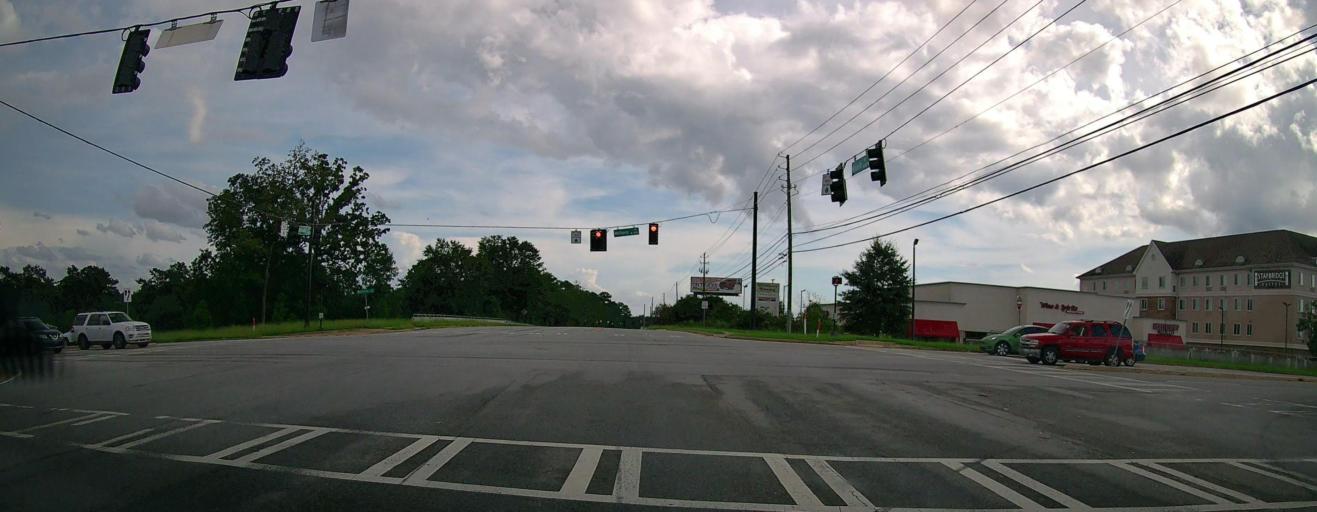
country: US
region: Alabama
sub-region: Russell County
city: Phenix City
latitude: 32.5399
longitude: -84.9666
